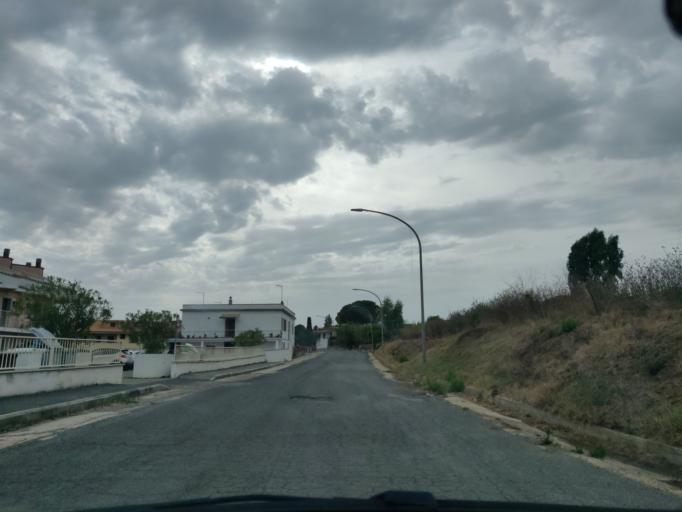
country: IT
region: Latium
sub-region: Citta metropolitana di Roma Capitale
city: Santa Marinella
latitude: 42.0420
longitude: 11.9041
